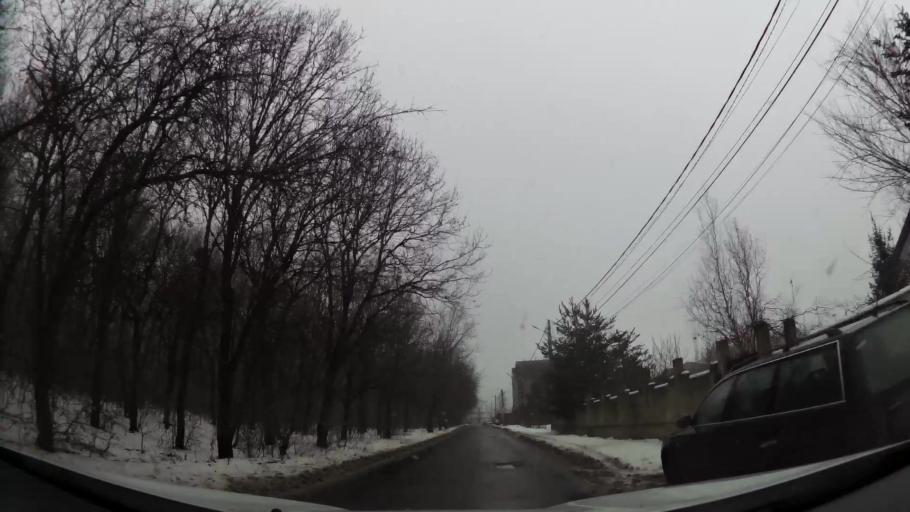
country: RO
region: Ilfov
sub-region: Comuna Chiajna
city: Rosu
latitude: 44.4571
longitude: 26.0037
